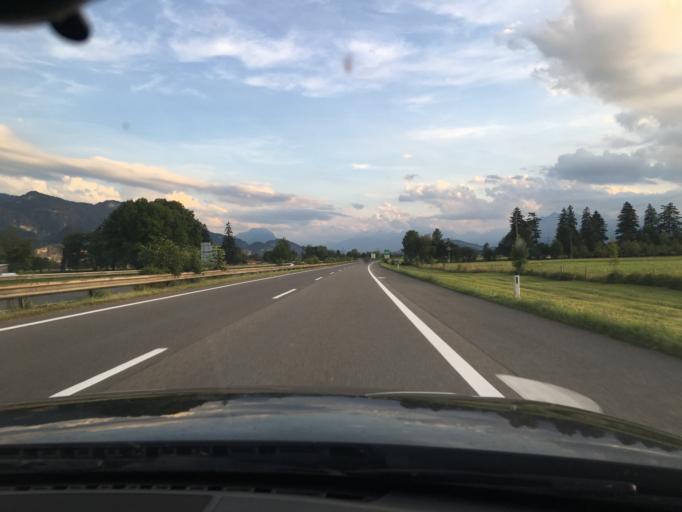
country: AT
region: Vorarlberg
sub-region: Politischer Bezirk Dornbirn
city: Dornbirn
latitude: 47.4071
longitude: 9.7034
